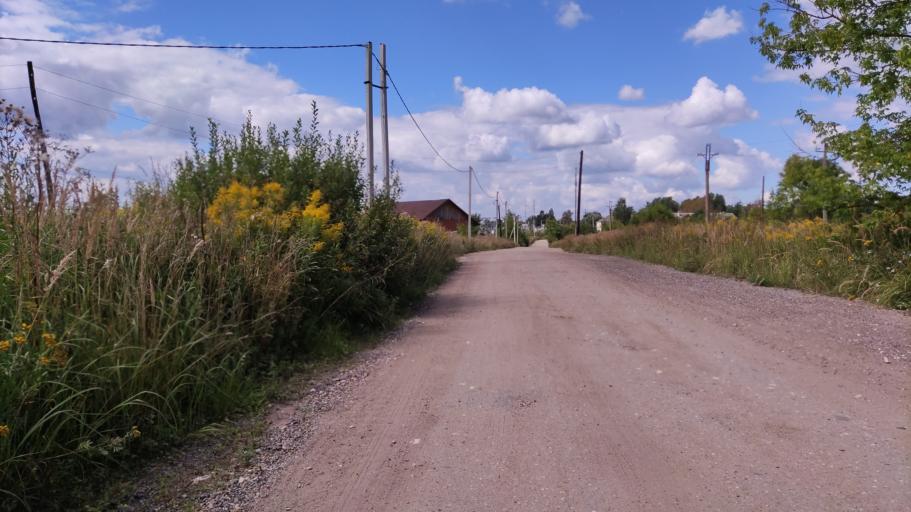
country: RU
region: Tverskaya
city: Rzhev
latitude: 56.2374
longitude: 34.3259
